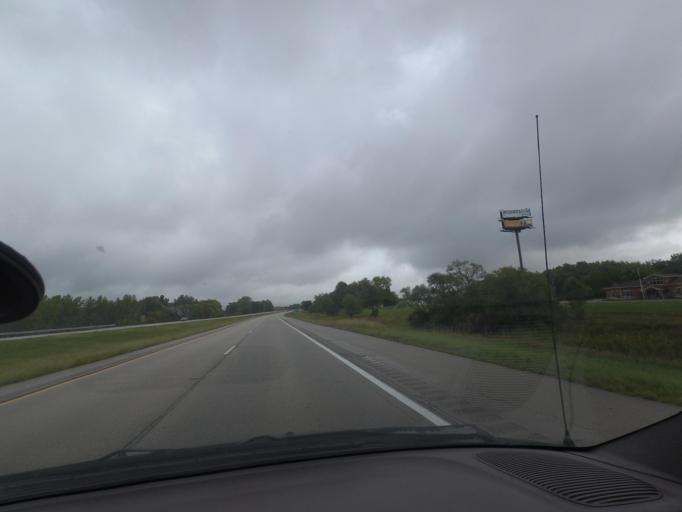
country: US
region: Illinois
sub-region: Piatt County
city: Monticello
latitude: 40.0501
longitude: -88.5727
